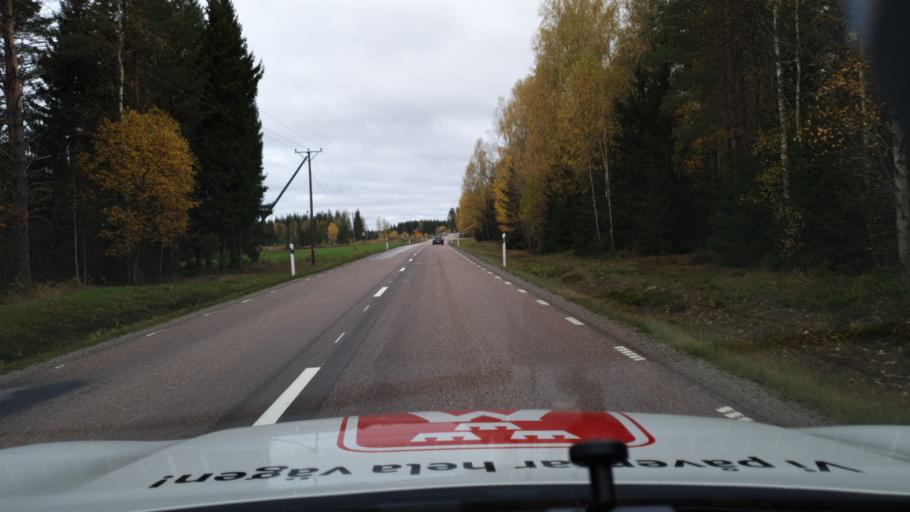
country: SE
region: Gaevleborg
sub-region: Gavle Kommun
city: Hedesunda
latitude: 60.4812
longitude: 16.9384
